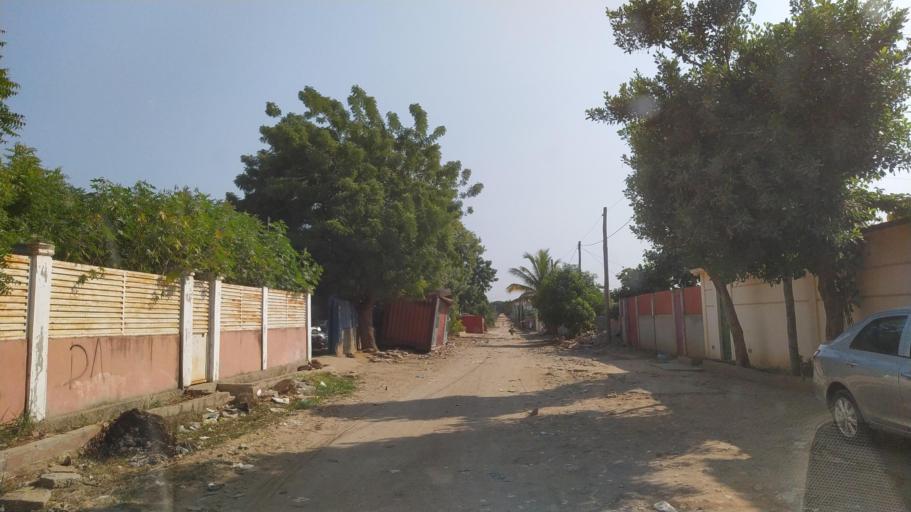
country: AO
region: Luanda
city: Luanda
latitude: -8.9404
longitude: 13.2550
